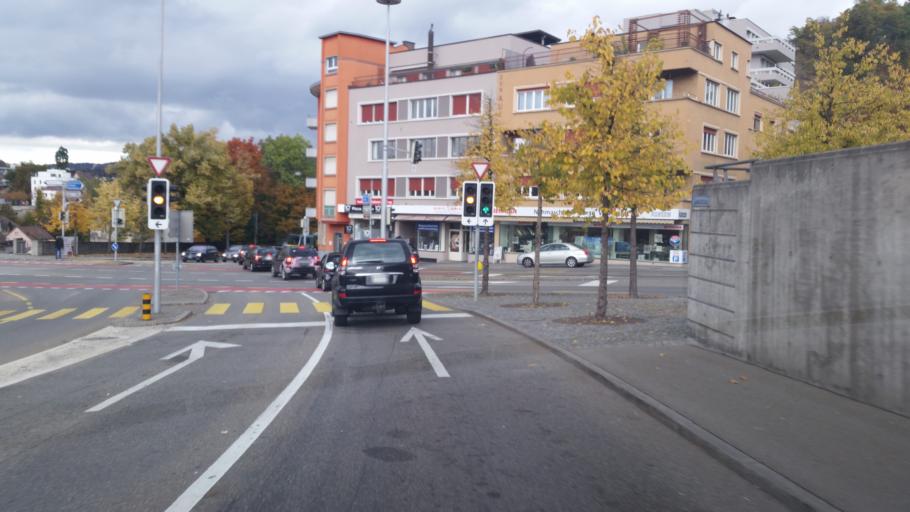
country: CH
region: Aargau
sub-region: Bezirk Baden
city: Wettingen
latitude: 47.4713
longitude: 8.3123
